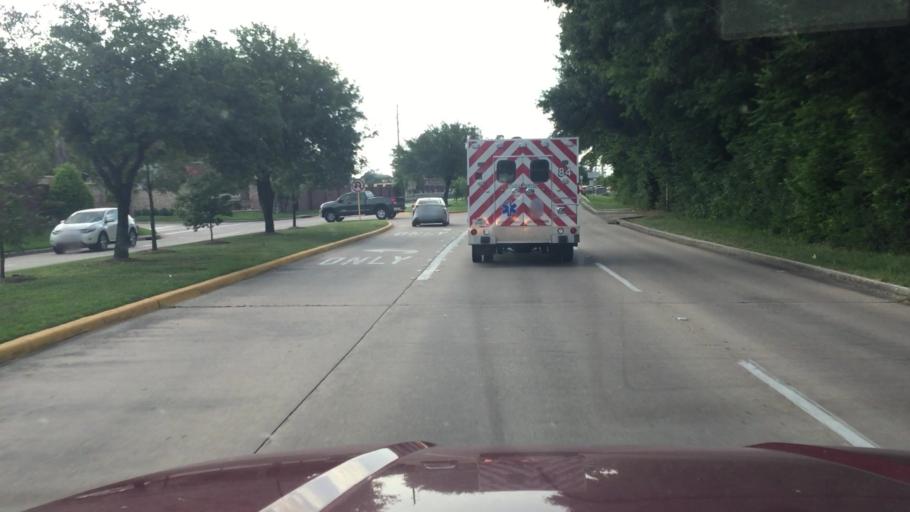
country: US
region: Texas
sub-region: Harris County
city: Tomball
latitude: 30.0272
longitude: -95.5304
